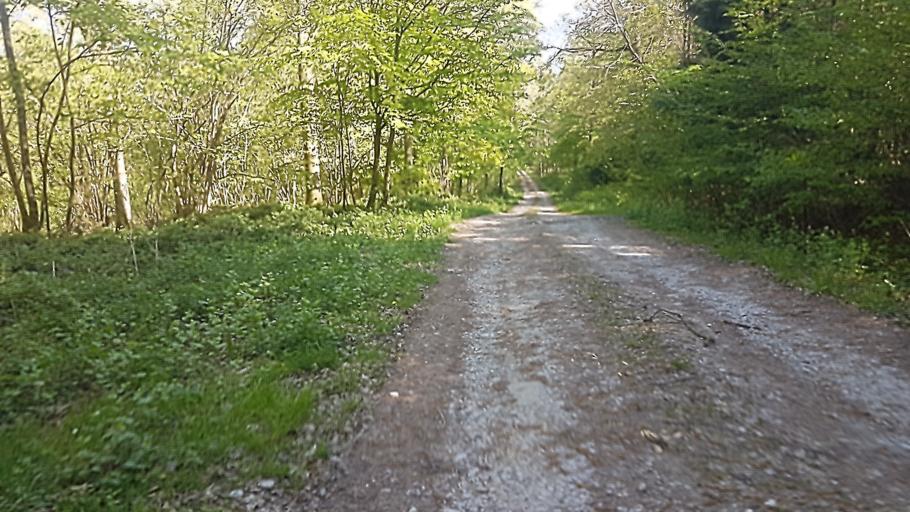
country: BE
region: Wallonia
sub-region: Province de Namur
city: Couvin
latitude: 50.0617
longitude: 4.5879
